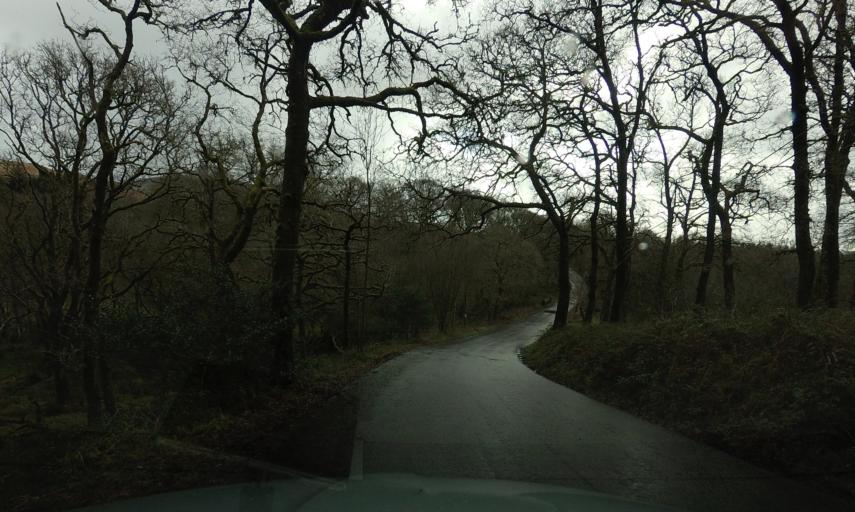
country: GB
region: Scotland
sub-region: West Dunbartonshire
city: Balloch
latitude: 56.1061
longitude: -4.5691
